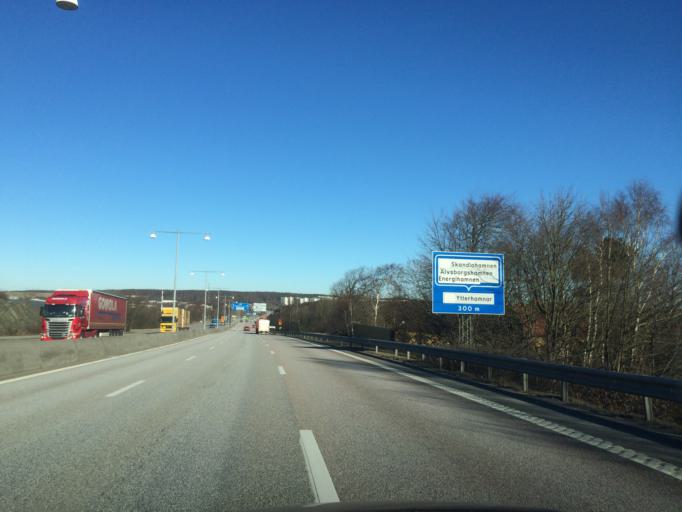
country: SE
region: Vaestra Goetaland
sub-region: Goteborg
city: Majorna
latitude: 57.6956
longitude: 11.8988
